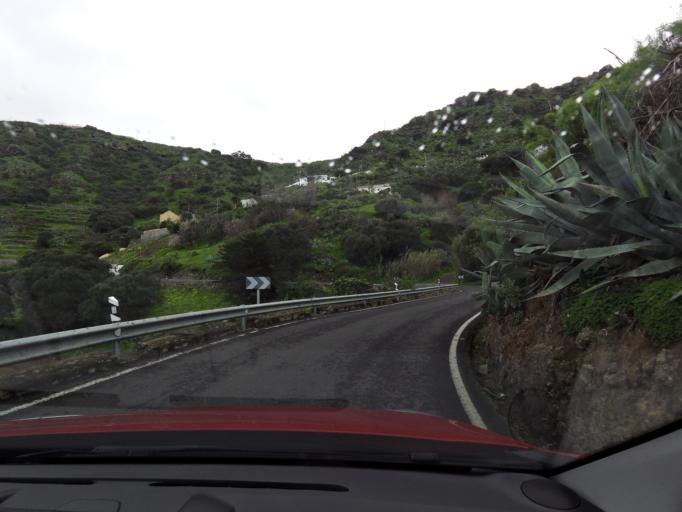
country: ES
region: Canary Islands
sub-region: Provincia de Las Palmas
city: Santa Brigida
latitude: 28.0209
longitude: -15.4744
